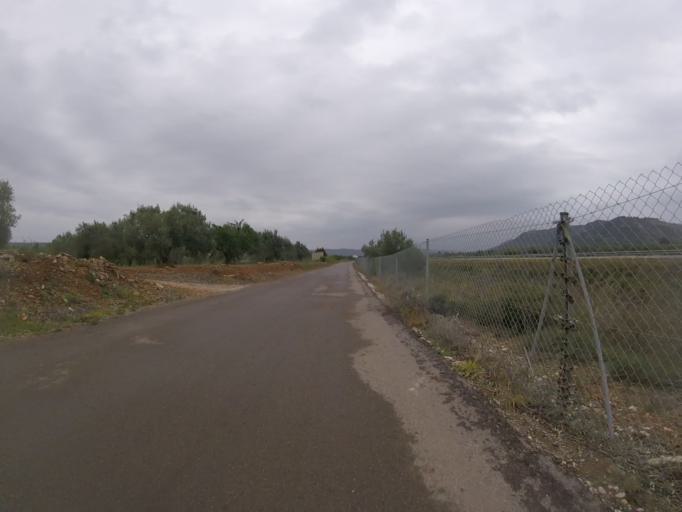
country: ES
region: Valencia
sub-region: Provincia de Castello
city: Alcala de Xivert
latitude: 40.2885
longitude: 0.2282
